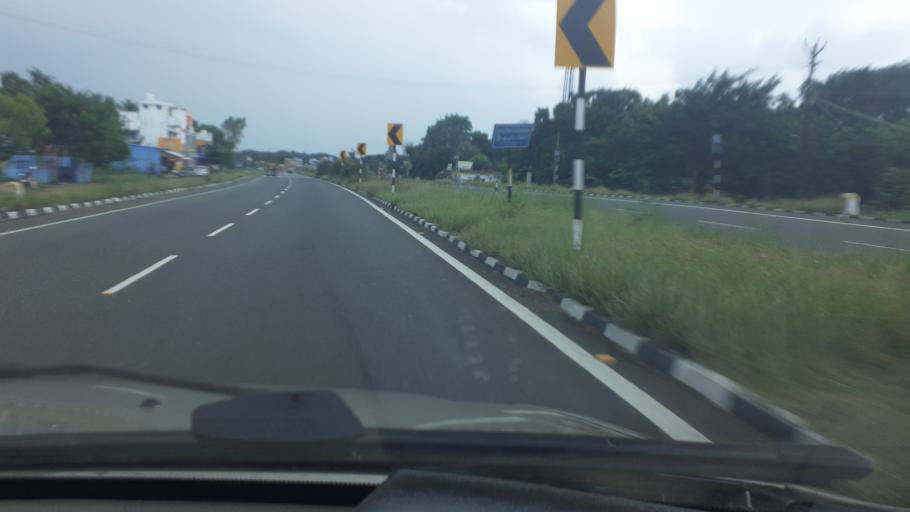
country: IN
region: Tamil Nadu
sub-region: Madurai
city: Kallupatti
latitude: 9.6958
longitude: 77.9718
